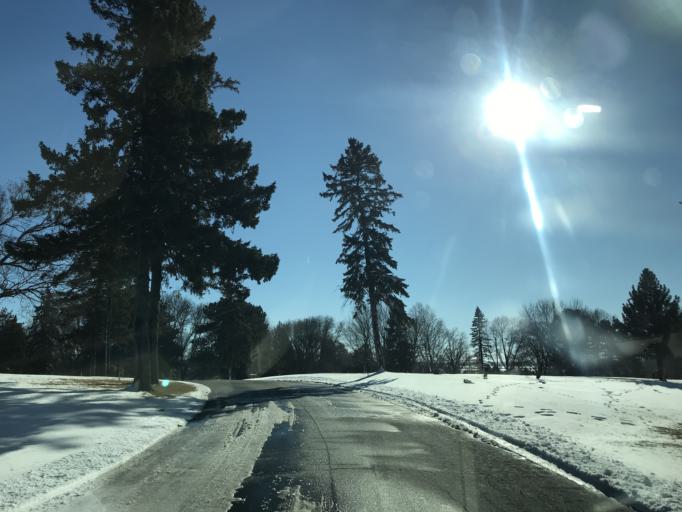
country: US
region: Wisconsin
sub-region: Dane County
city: Monona
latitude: 43.0500
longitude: -89.3200
